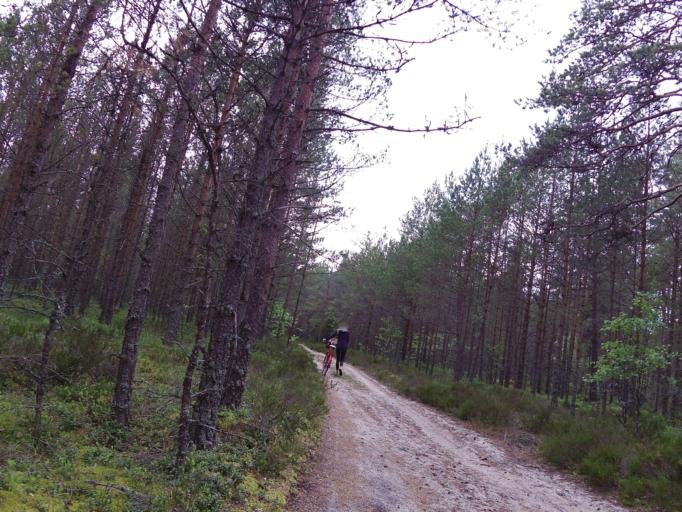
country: EE
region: Harju
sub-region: Paldiski linn
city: Paldiski
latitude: 59.2423
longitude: 23.7458
